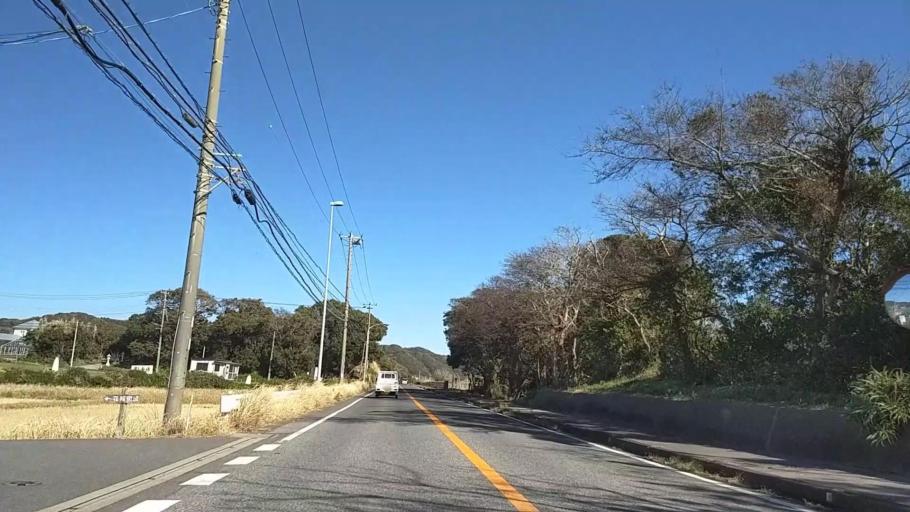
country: JP
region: Chiba
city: Kawaguchi
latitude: 35.0450
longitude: 140.0242
